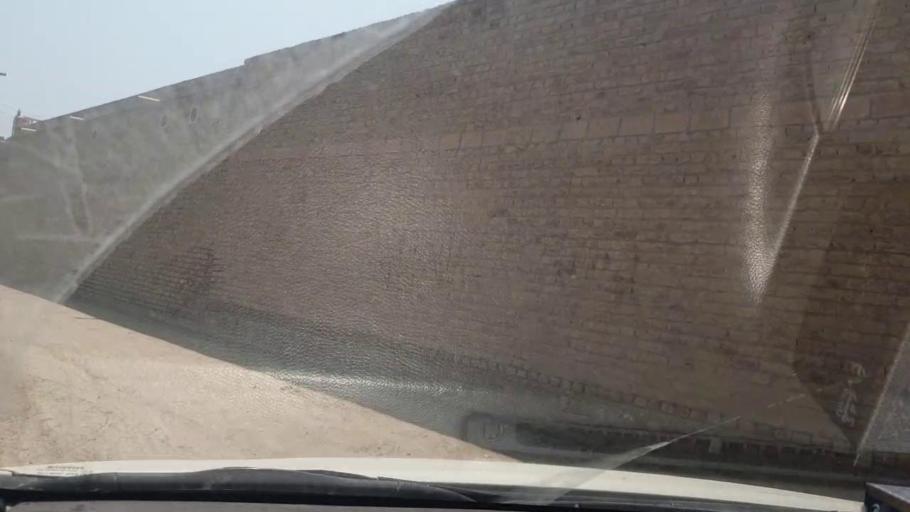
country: PK
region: Sindh
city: Shikarpur
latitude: 27.9320
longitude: 68.6635
